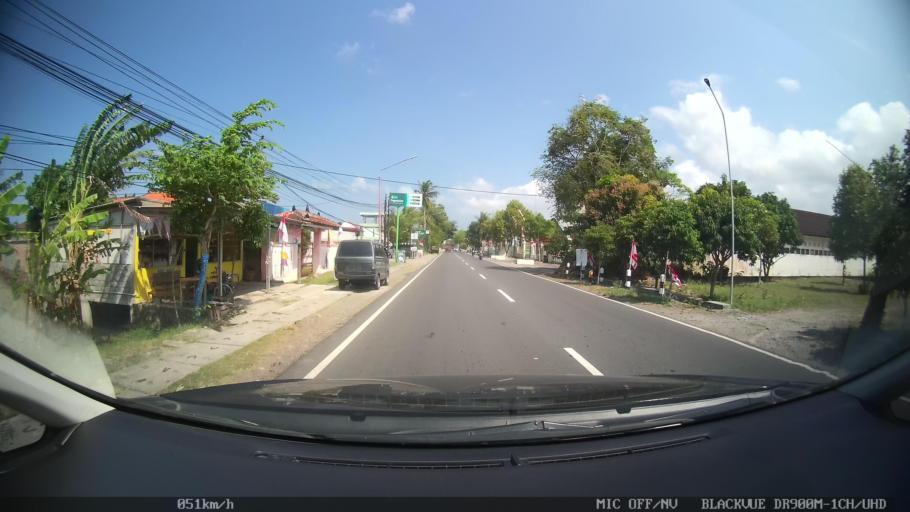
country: ID
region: Daerah Istimewa Yogyakarta
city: Srandakan
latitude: -7.8949
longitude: 110.1493
